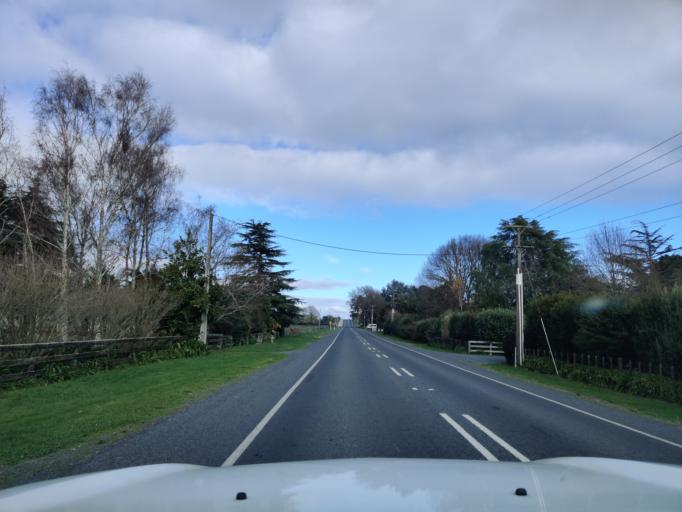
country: NZ
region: Waikato
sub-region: Waipa District
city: Cambridge
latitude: -37.8625
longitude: 175.4390
